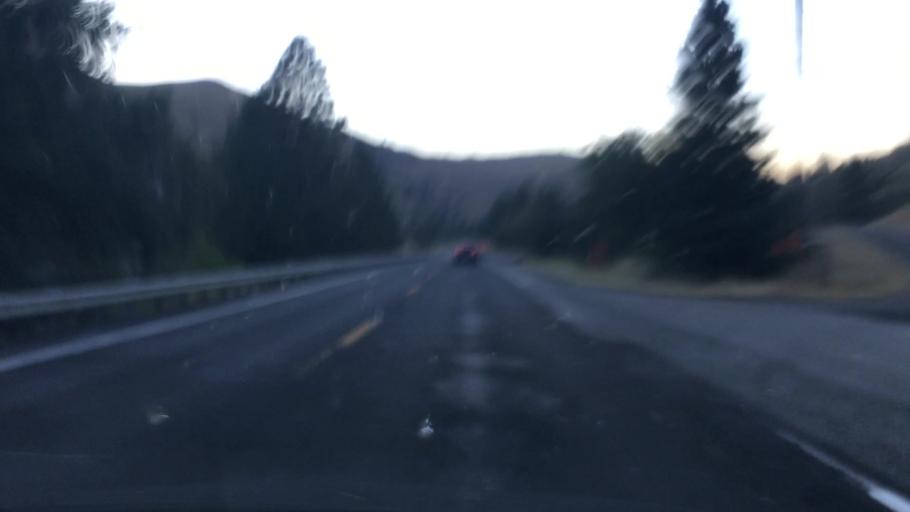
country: US
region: Idaho
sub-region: Valley County
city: McCall
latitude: 45.2950
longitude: -116.3584
